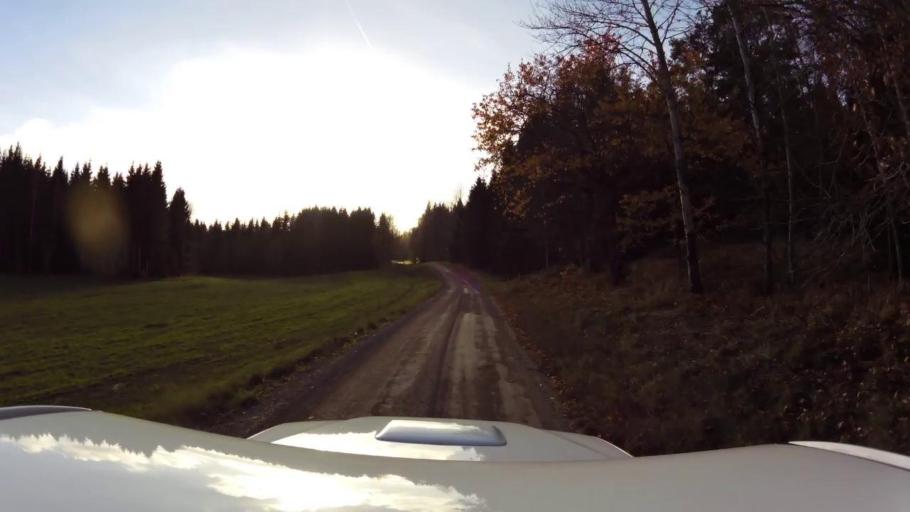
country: SE
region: OEstergoetland
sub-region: Linkopings Kommun
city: Vikingstad
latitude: 58.2189
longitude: 15.4441
